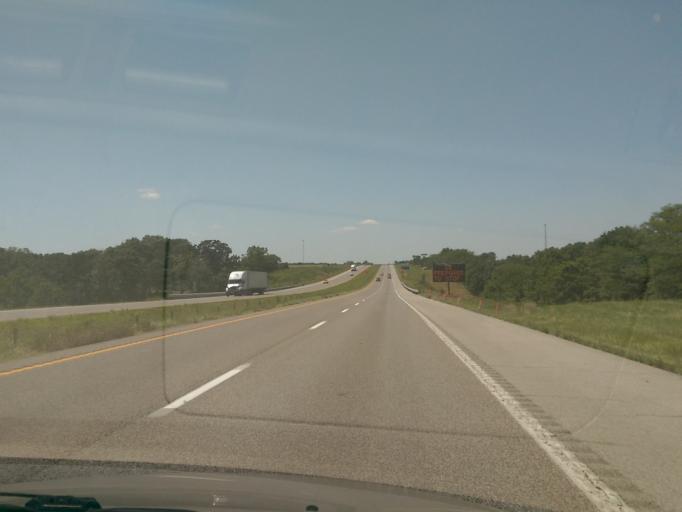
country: US
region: Missouri
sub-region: Saline County
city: Marshall
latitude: 38.9522
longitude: -93.0736
